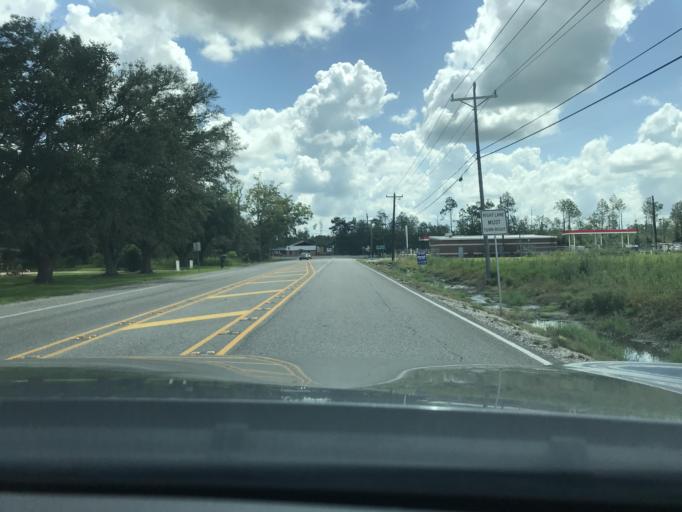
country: US
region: Louisiana
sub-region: Calcasieu Parish
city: Moss Bluff
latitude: 30.3445
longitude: -93.2022
